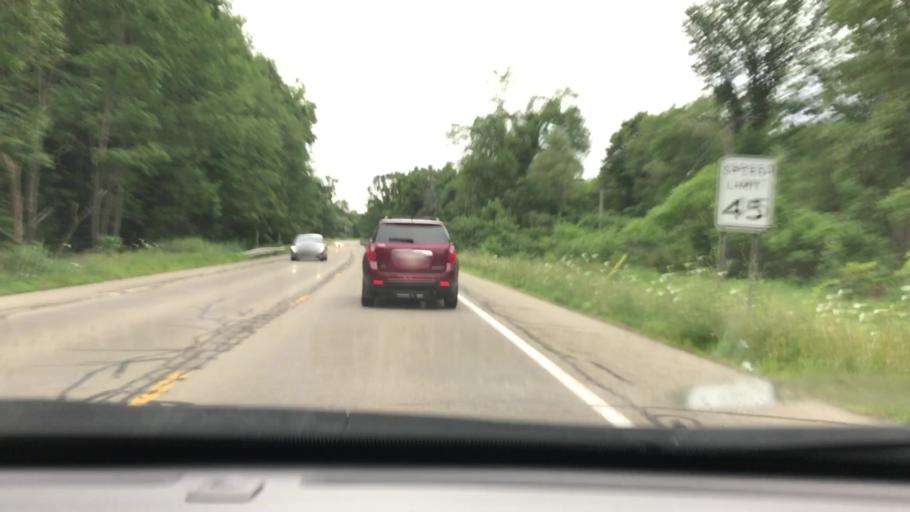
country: US
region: New York
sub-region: Erie County
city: Springville
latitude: 42.4140
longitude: -78.6911
